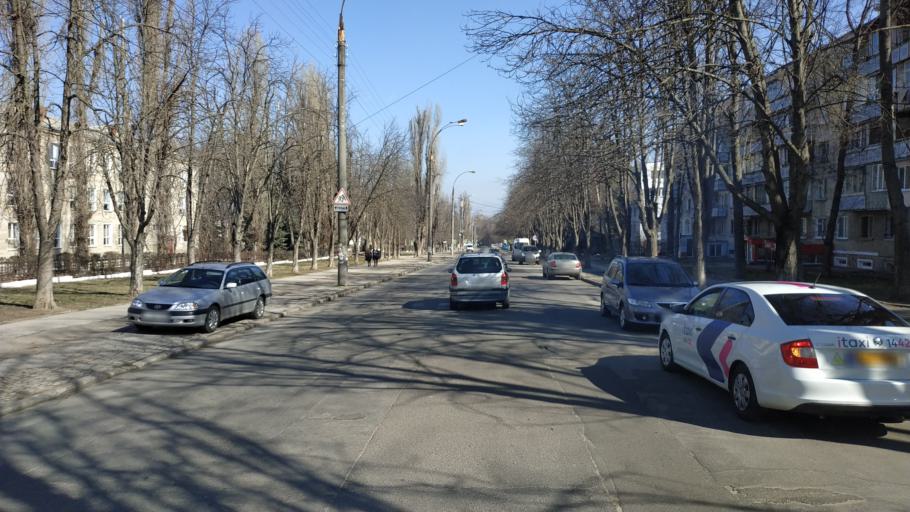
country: MD
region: Chisinau
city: Vatra
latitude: 47.0298
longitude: 28.7892
